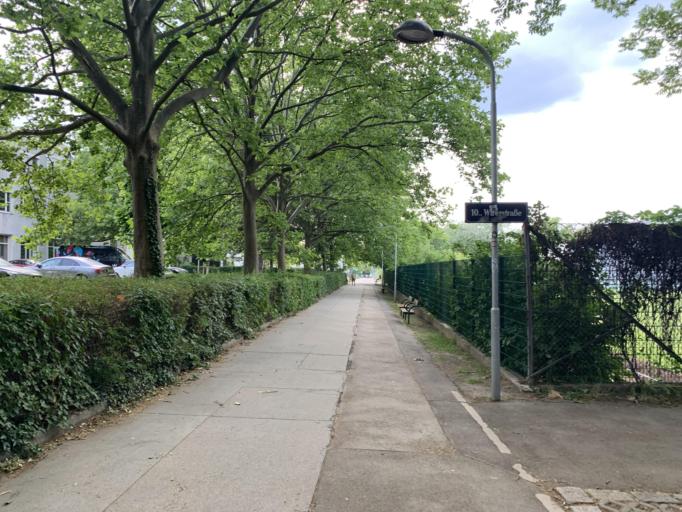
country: AT
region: Vienna
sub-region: Wien Stadt
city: Vienna
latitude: 48.1667
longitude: 16.3772
